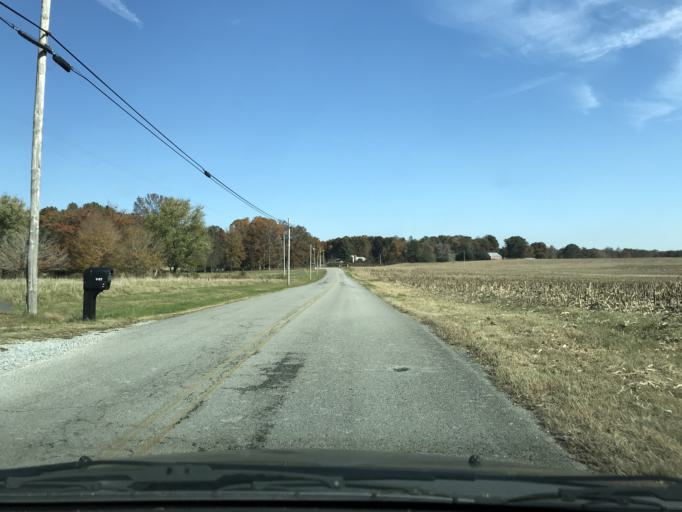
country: US
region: Tennessee
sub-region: Coffee County
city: Tullahoma
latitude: 35.4039
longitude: -86.1576
